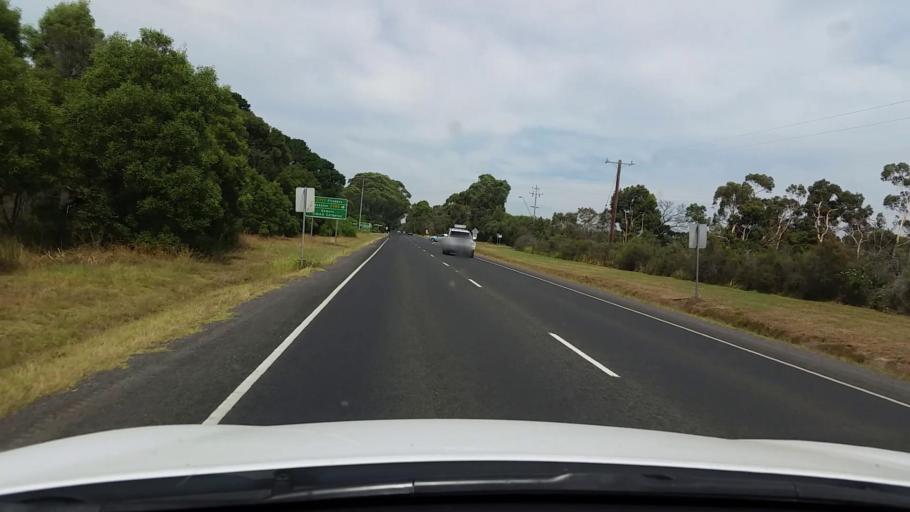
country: AU
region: Victoria
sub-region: Mornington Peninsula
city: Balnarring
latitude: -38.3598
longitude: 145.1466
